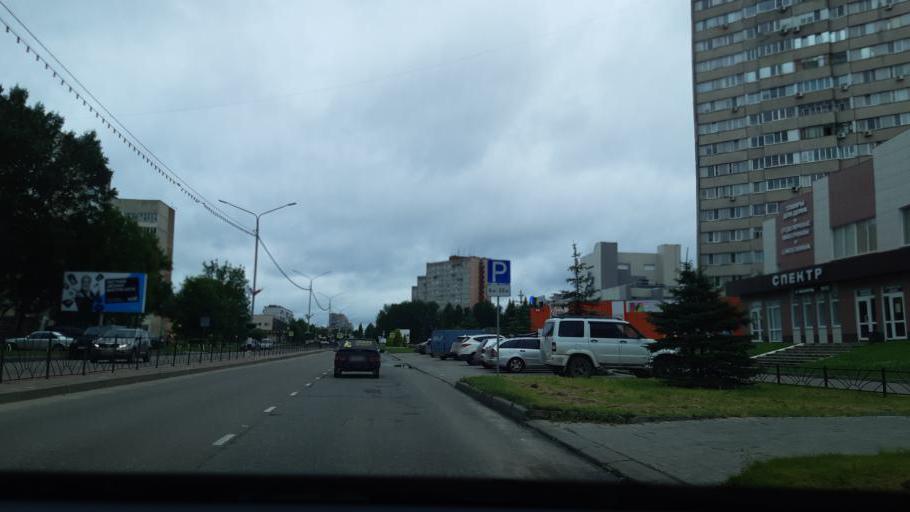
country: RU
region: Smolensk
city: Desnogorsk
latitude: 54.1498
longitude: 33.2855
